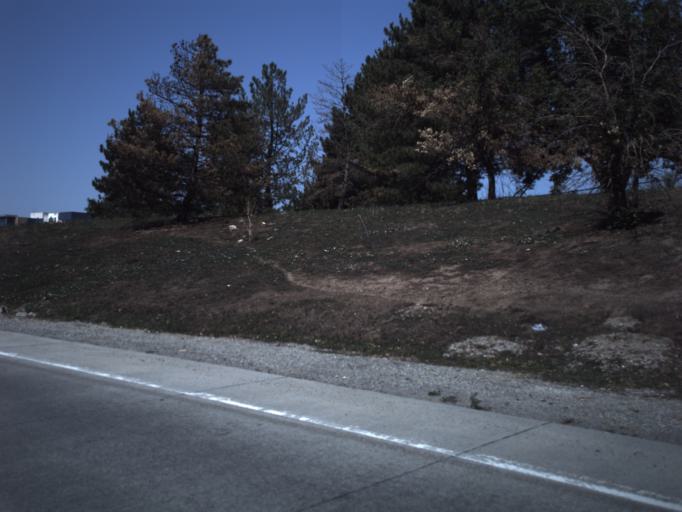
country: US
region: Utah
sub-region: Salt Lake County
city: Willard
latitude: 40.7213
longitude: -111.8526
